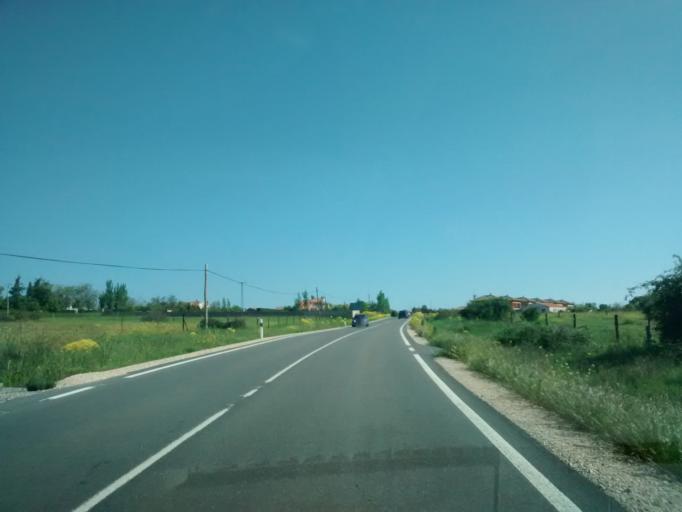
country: ES
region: Castille and Leon
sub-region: Provincia de Segovia
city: Torrecaballeros
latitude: 40.9869
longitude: -4.0239
